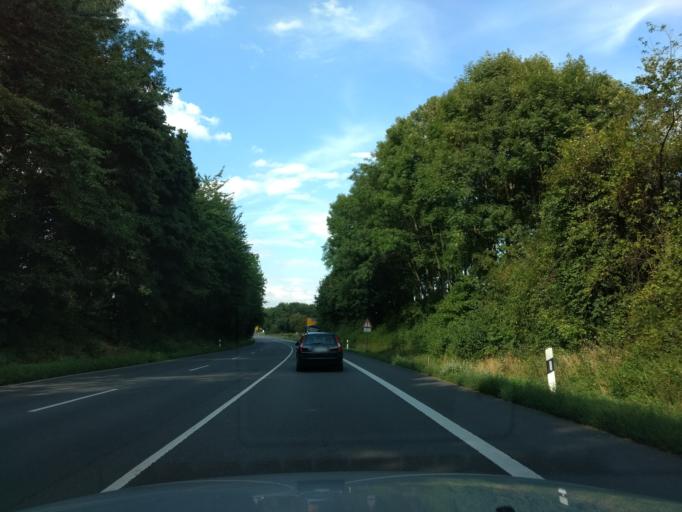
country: DE
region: North Rhine-Westphalia
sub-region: Regierungsbezirk Dusseldorf
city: Grevenbroich
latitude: 51.0983
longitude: 6.5631
